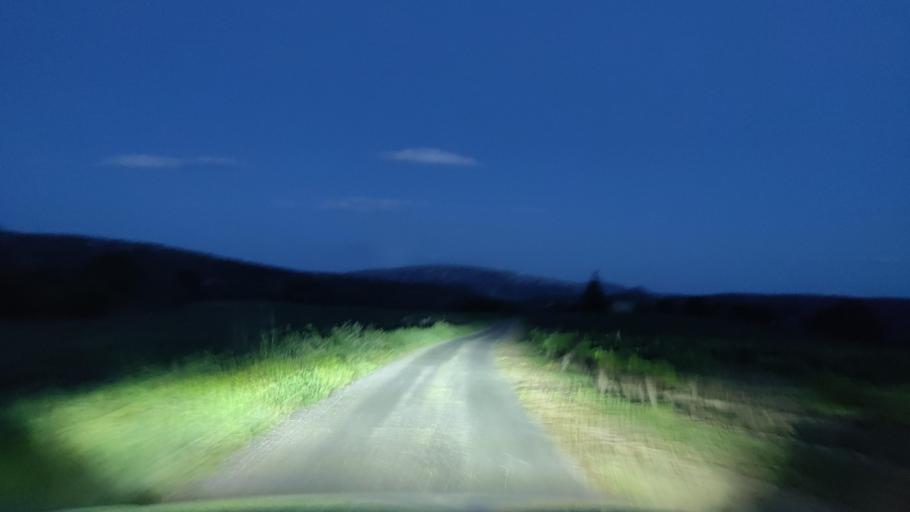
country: FR
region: Languedoc-Roussillon
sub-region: Departement des Pyrenees-Orientales
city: Estagel
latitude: 42.8774
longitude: 2.7288
